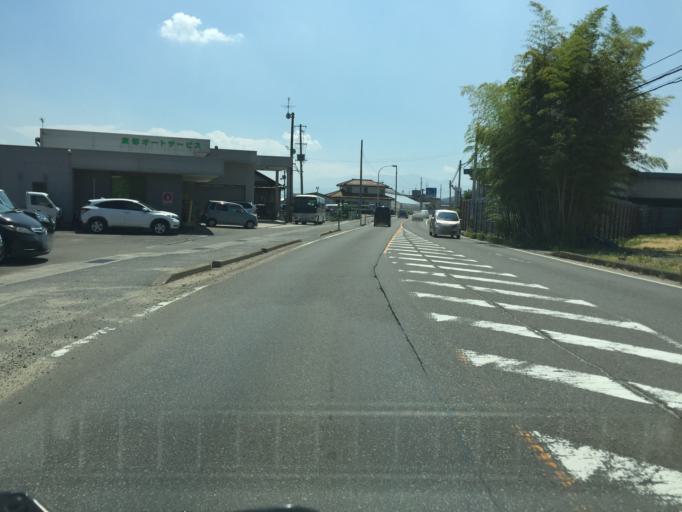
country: JP
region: Fukushima
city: Hobaramachi
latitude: 37.7915
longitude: 140.5133
